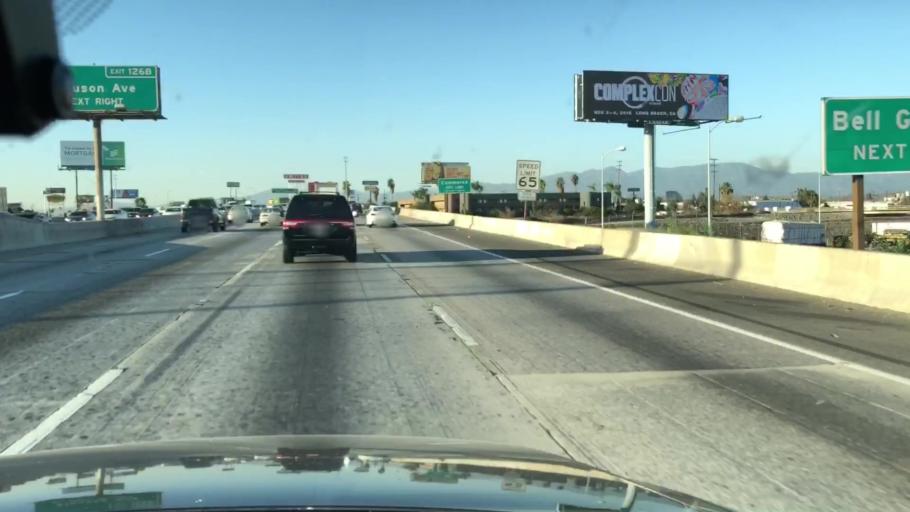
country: US
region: California
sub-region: Los Angeles County
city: Pico Rivera
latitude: 33.9708
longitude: -118.1226
